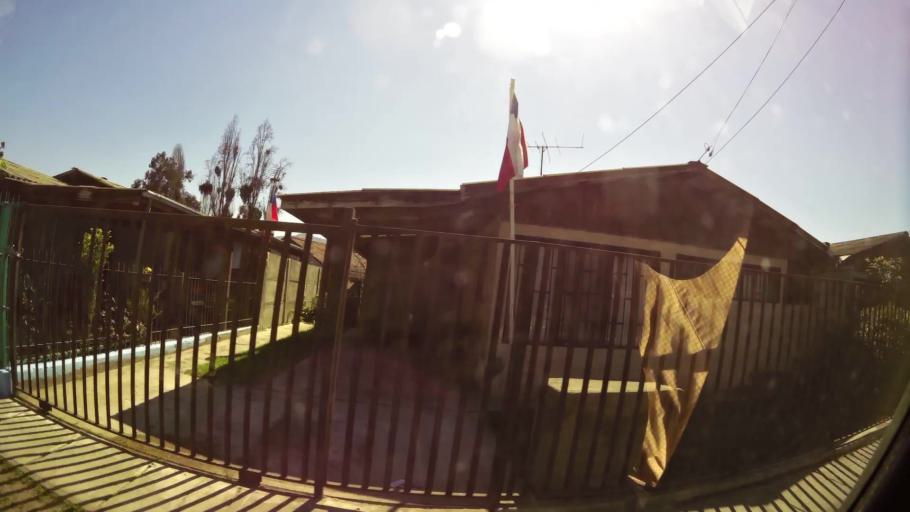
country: CL
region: Santiago Metropolitan
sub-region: Provincia de Talagante
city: Penaflor
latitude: -33.6012
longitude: -70.8881
